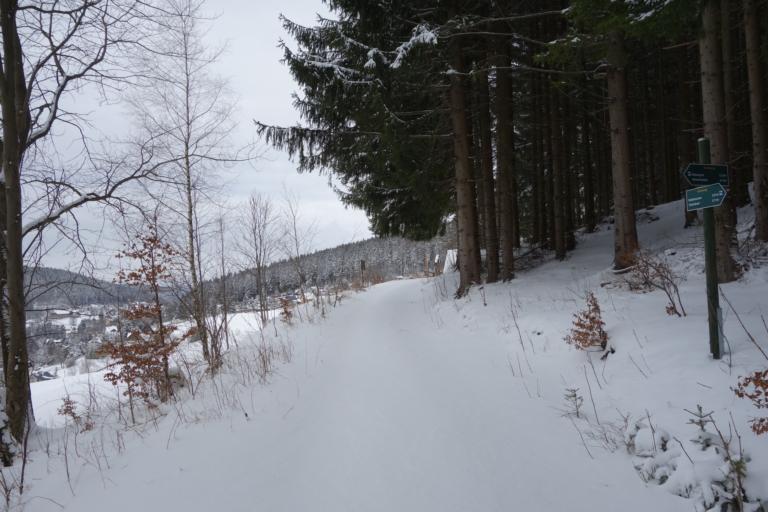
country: DE
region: Saxony
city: Rittersgrun
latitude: 50.4611
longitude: 12.8200
